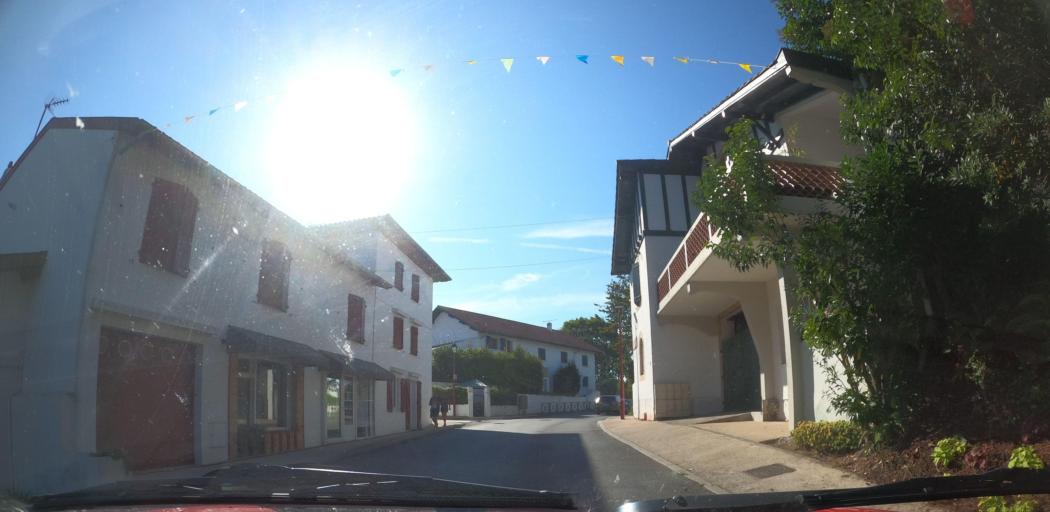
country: FR
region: Aquitaine
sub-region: Departement des Pyrenees-Atlantiques
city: Arbonne
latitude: 43.4313
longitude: -1.5506
